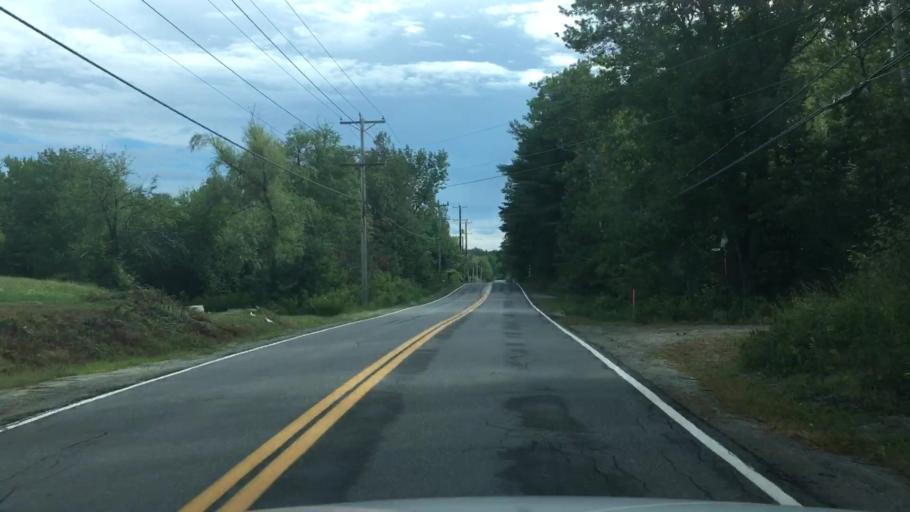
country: US
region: Maine
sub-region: Hancock County
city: Ellsworth
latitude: 44.4884
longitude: -68.4200
